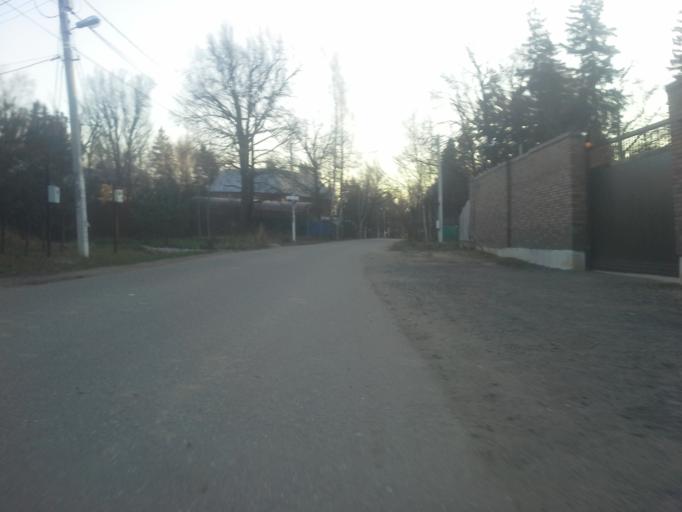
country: RU
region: Moskovskaya
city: Lesnoy Gorodok
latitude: 55.6391
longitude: 37.2058
